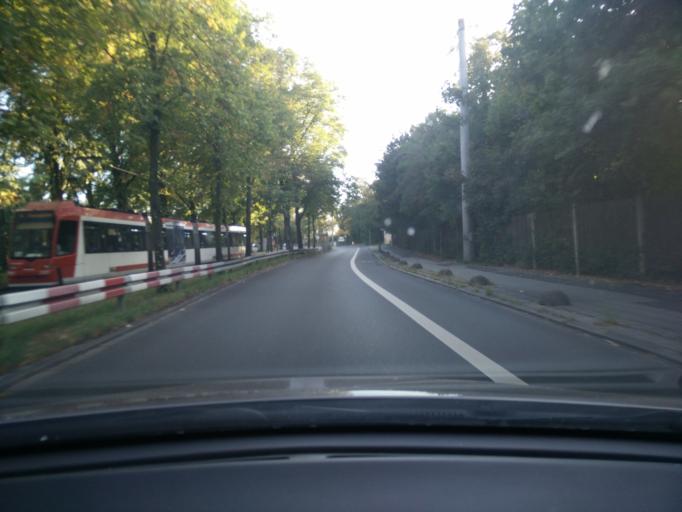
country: DE
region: Bavaria
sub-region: Regierungsbezirk Mittelfranken
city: Nuernberg
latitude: 49.4208
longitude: 11.0841
